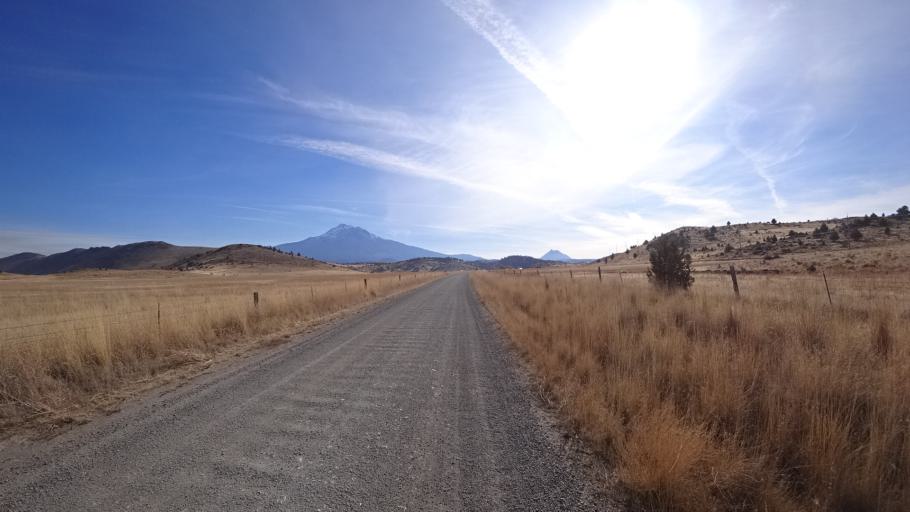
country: US
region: California
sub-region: Siskiyou County
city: Weed
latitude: 41.5095
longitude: -122.4630
